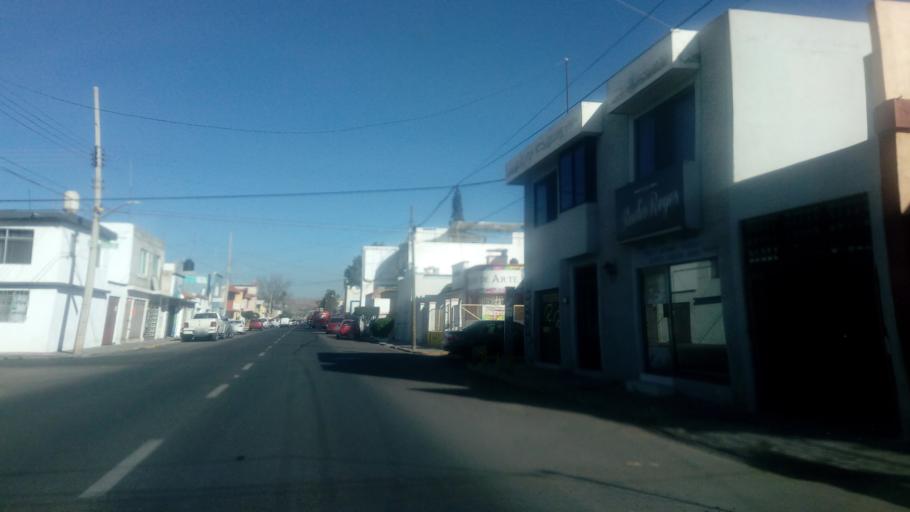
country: MX
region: Durango
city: Victoria de Durango
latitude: 24.0294
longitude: -104.6586
